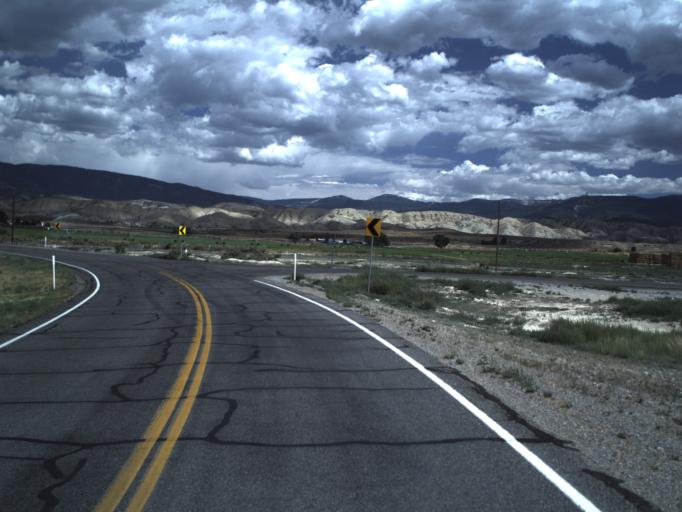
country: US
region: Utah
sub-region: Sanpete County
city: Centerfield
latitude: 39.1344
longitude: -111.7753
